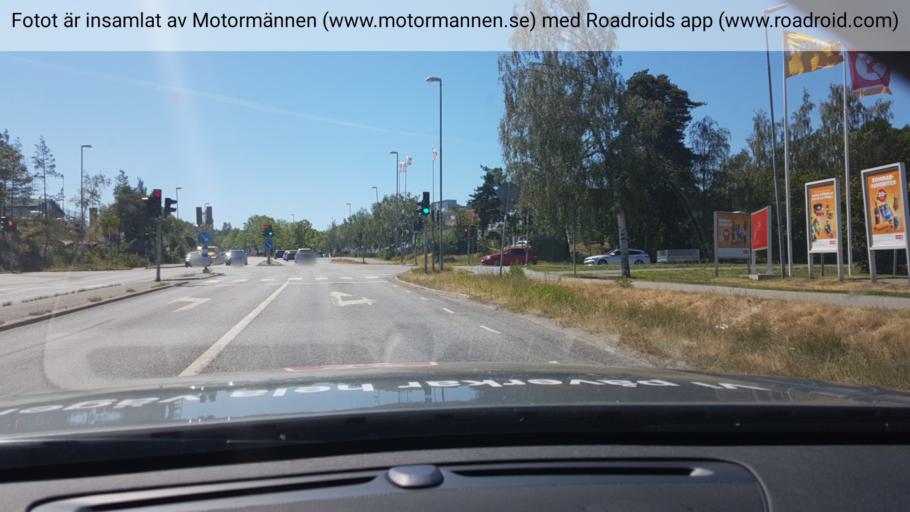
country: SE
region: Stockholm
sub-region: Haninge Kommun
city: Haninge
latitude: 59.1776
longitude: 18.1622
